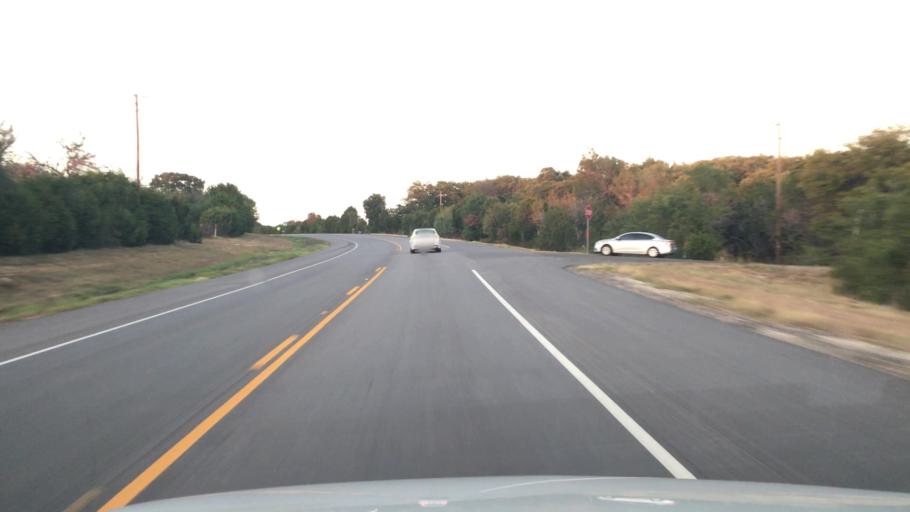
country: US
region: Texas
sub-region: Somervell County
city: Glen Rose
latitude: 32.1948
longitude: -97.8134
